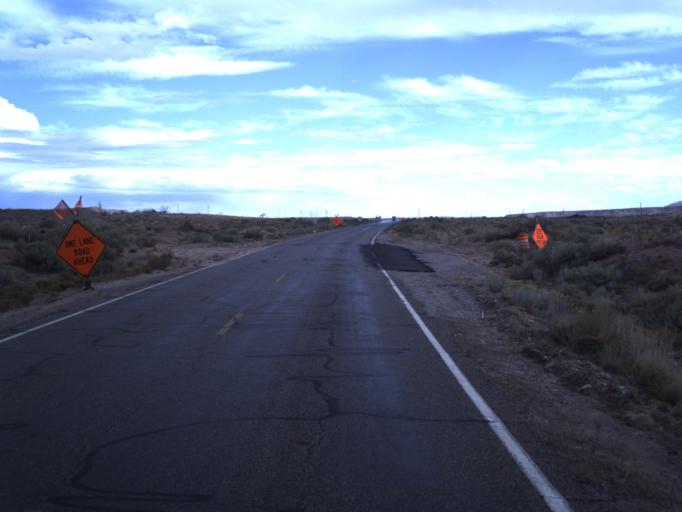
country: US
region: Utah
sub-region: San Juan County
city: Blanding
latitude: 37.2328
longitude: -109.2185
